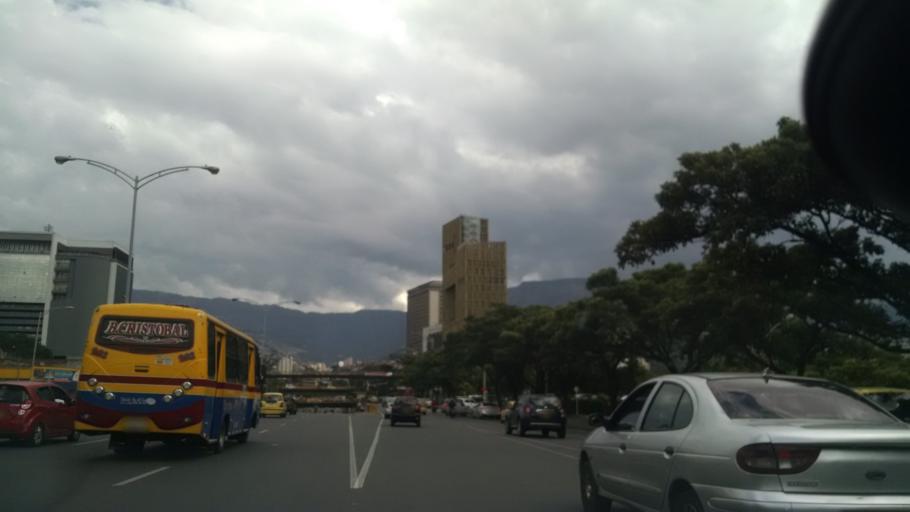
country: CO
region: Antioquia
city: Medellin
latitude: 6.2470
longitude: -75.5778
